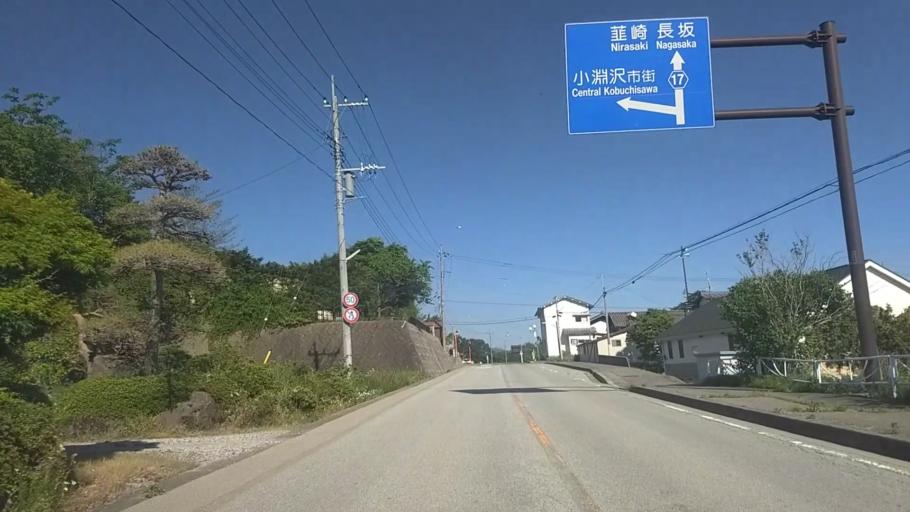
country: JP
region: Nagano
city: Chino
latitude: 35.8616
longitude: 138.3007
